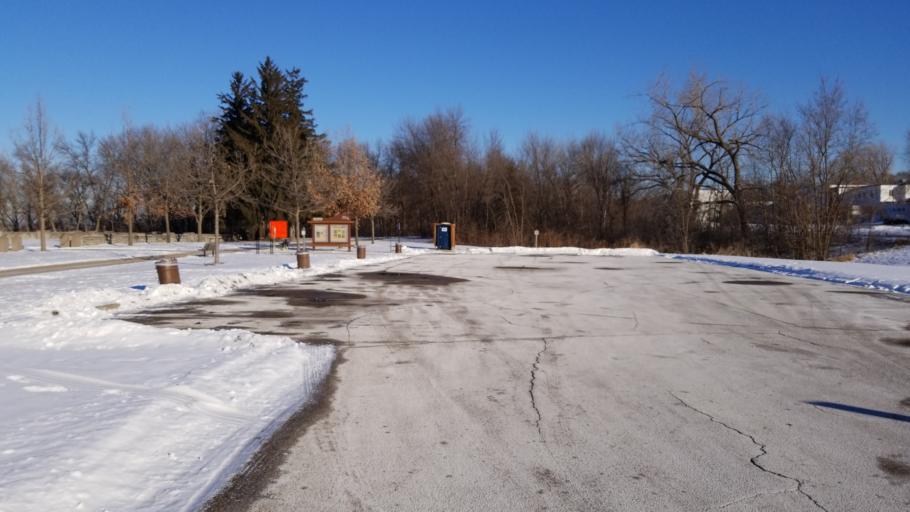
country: US
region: Minnesota
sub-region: Dakota County
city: Mendota Heights
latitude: 44.8668
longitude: -93.1735
